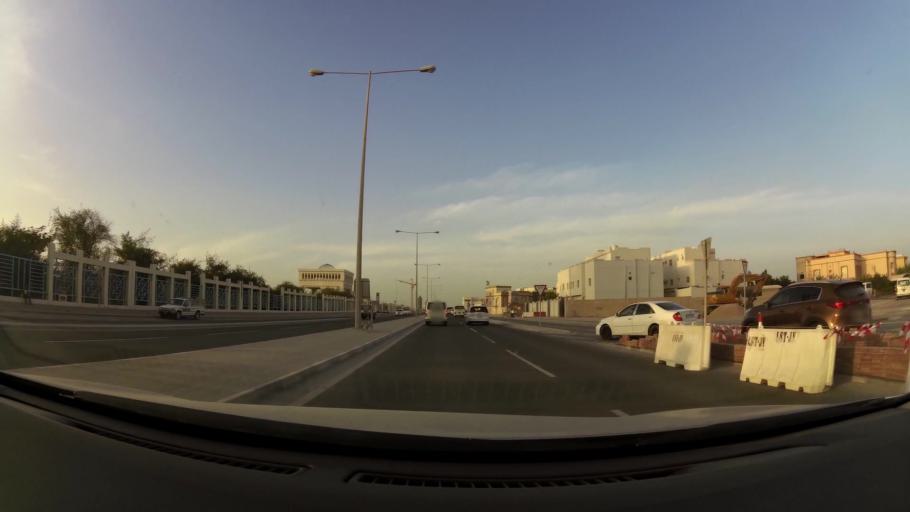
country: QA
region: Al Wakrah
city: Al Wakrah
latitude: 25.1668
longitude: 51.5906
